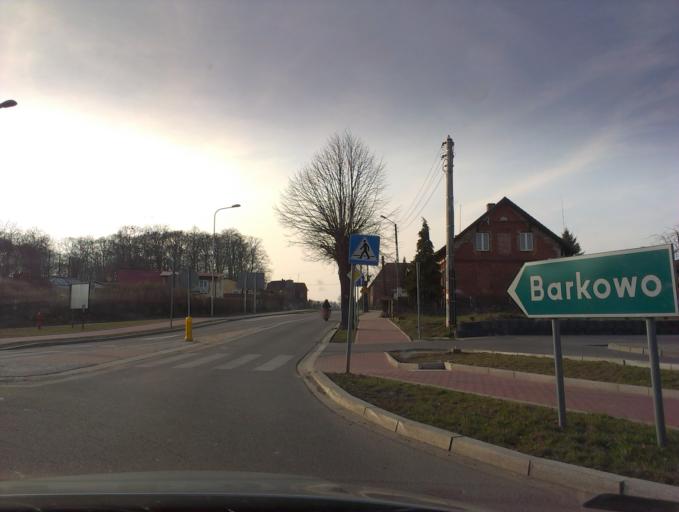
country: PL
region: Pomeranian Voivodeship
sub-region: Powiat czluchowski
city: Debrzno
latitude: 53.5410
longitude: 17.2358
